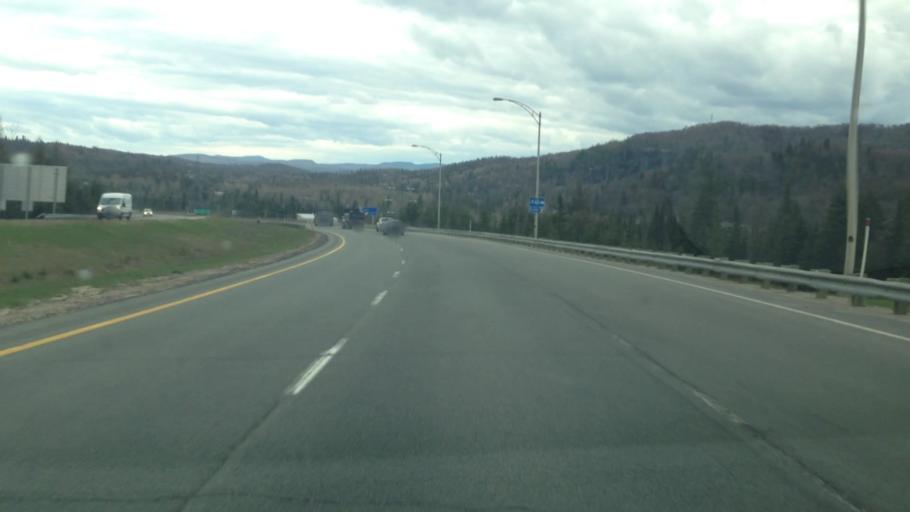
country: CA
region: Quebec
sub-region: Laurentides
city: Sainte-Agathe-des-Monts
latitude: 46.0467
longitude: -74.2657
